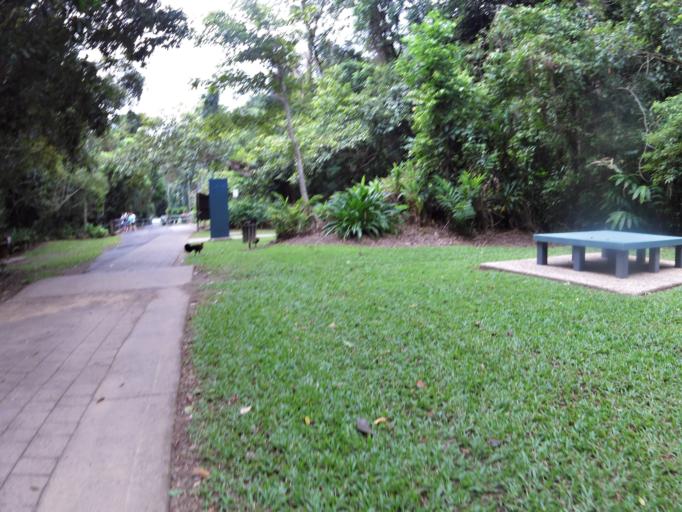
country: AU
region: Queensland
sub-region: Cairns
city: Woree
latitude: -16.9624
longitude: 145.6791
